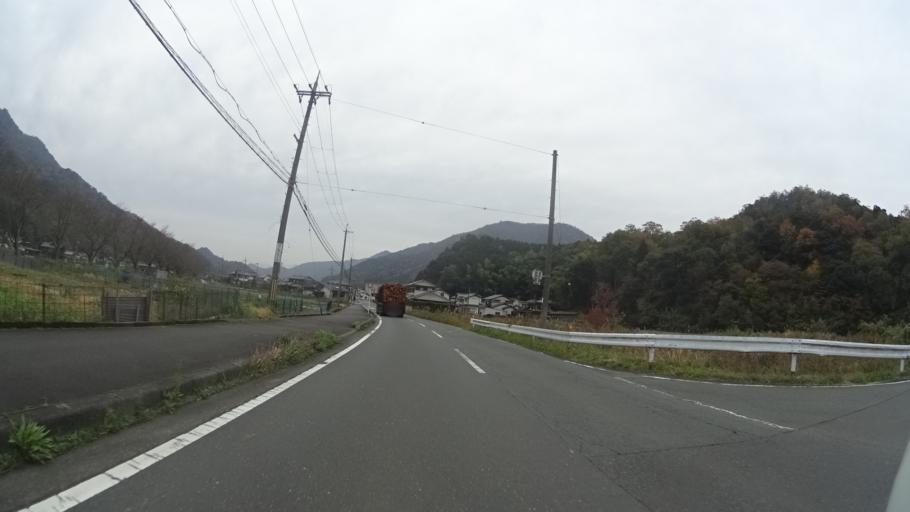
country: JP
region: Kyoto
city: Maizuru
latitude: 35.4978
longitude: 135.4363
